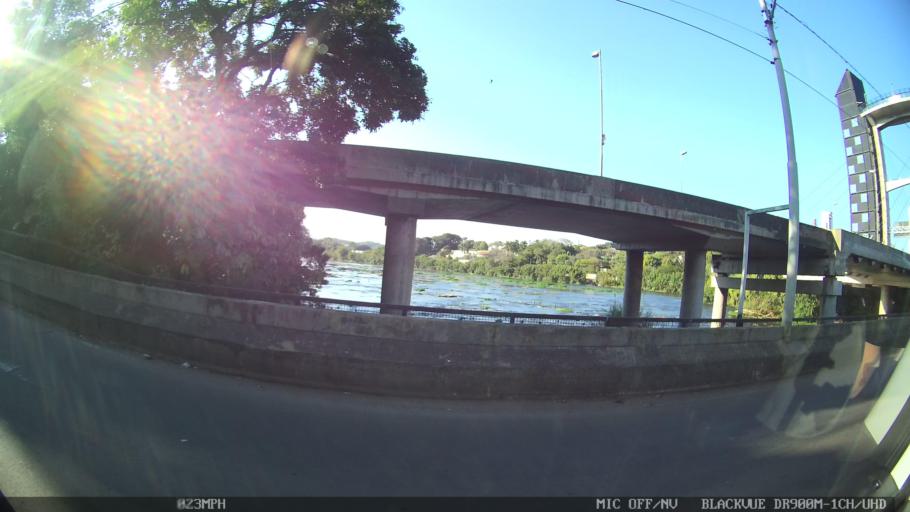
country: BR
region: Sao Paulo
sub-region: Piracicaba
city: Piracicaba
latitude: -22.7141
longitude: -47.6522
